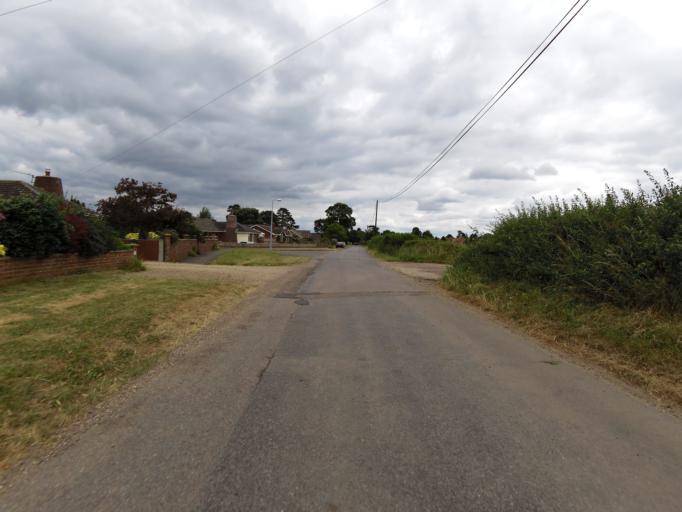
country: GB
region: England
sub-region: Suffolk
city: Bungay
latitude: 52.4484
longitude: 1.4142
